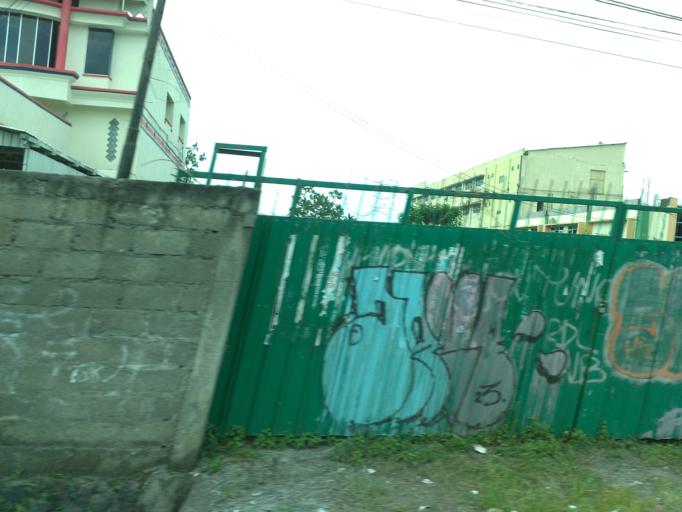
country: ID
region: Central Java
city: Klaten
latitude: -7.6864
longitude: 110.6382
